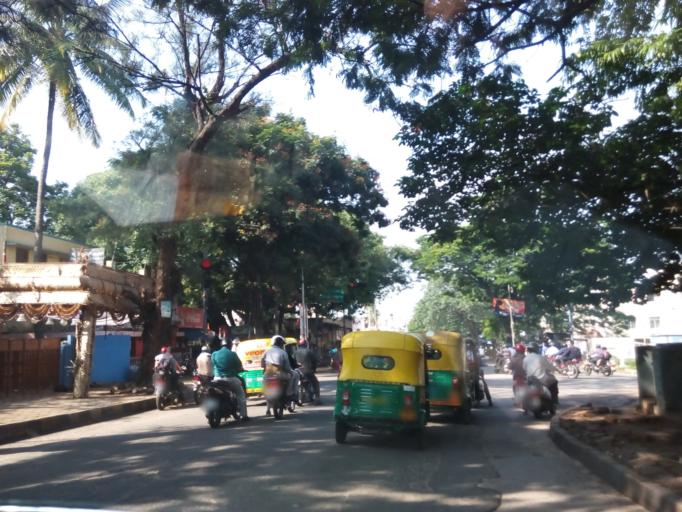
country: IN
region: Karnataka
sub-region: Bangalore Urban
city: Bangalore
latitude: 12.9909
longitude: 77.5997
